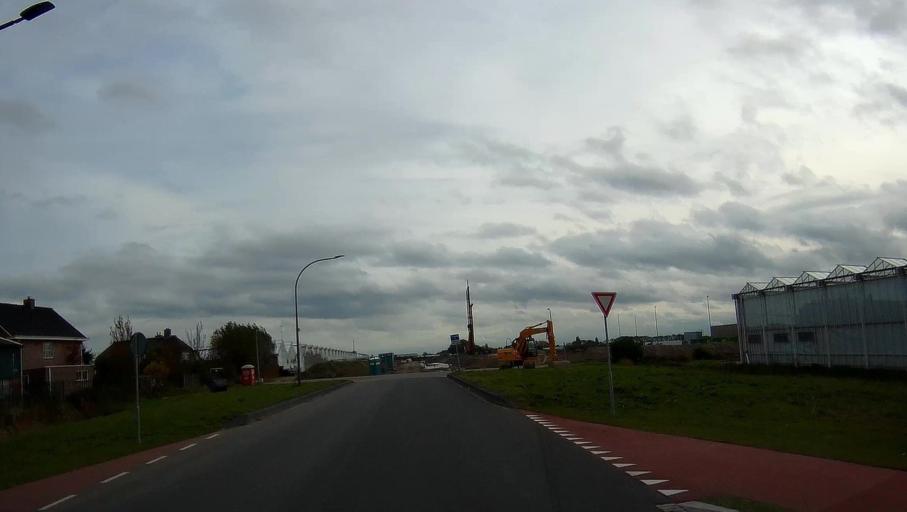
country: NL
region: South Holland
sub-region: Gemeente Zwijndrecht
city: Heerjansdam
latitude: 51.8658
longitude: 4.5680
